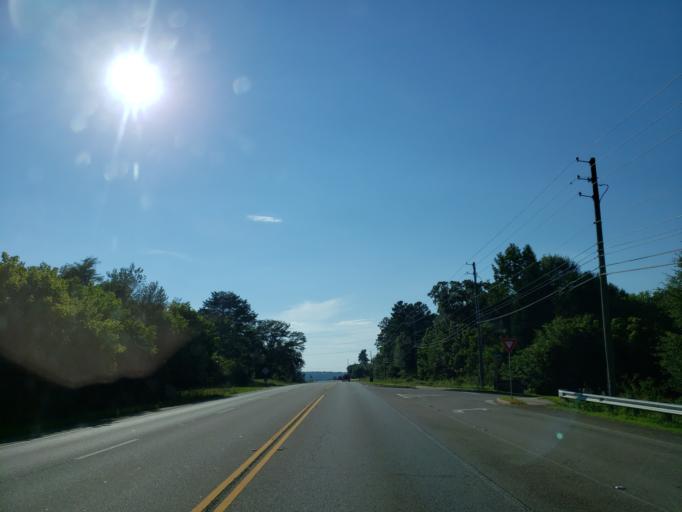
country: US
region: Georgia
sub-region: Cherokee County
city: Ball Ground
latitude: 34.2531
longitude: -84.3135
